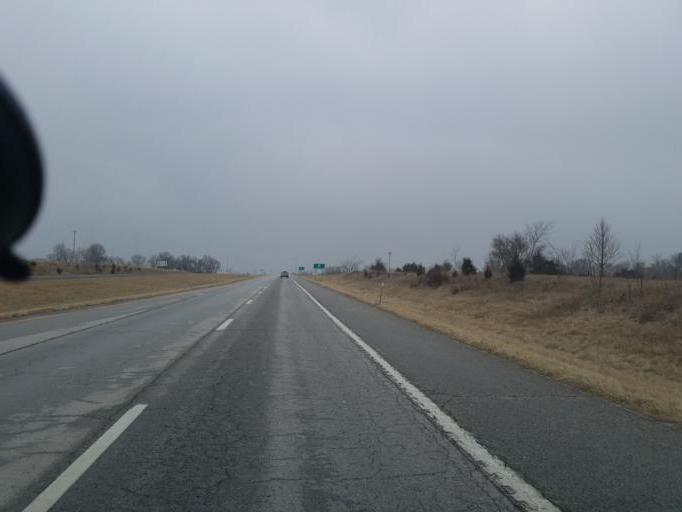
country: US
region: Missouri
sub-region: Macon County
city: La Plata
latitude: 39.9022
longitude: -92.4726
